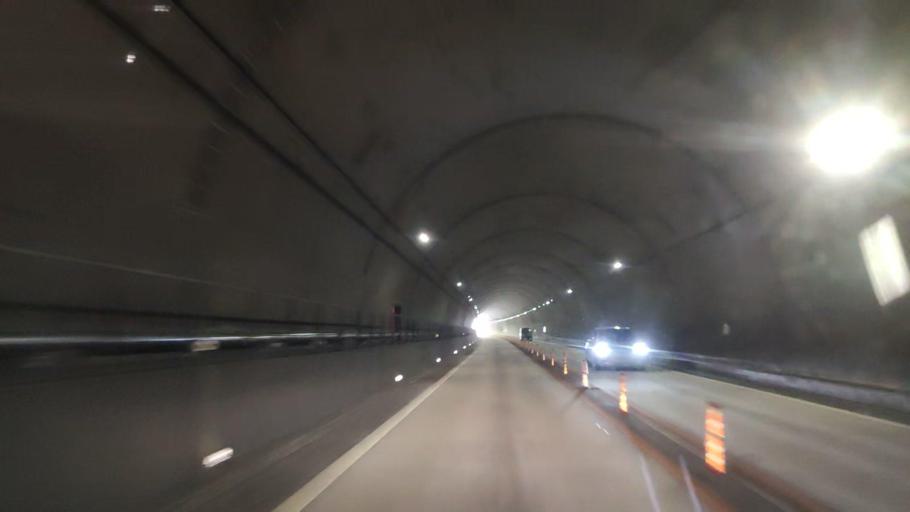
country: JP
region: Ehime
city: Hojo
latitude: 34.0852
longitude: 132.9778
